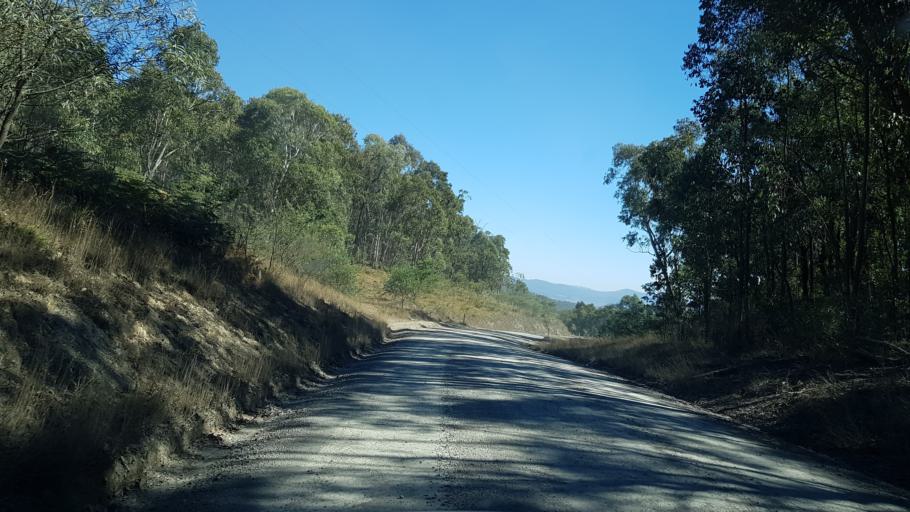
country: AU
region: Victoria
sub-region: Mansfield
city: Mansfield
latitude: -36.8449
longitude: 146.5027
